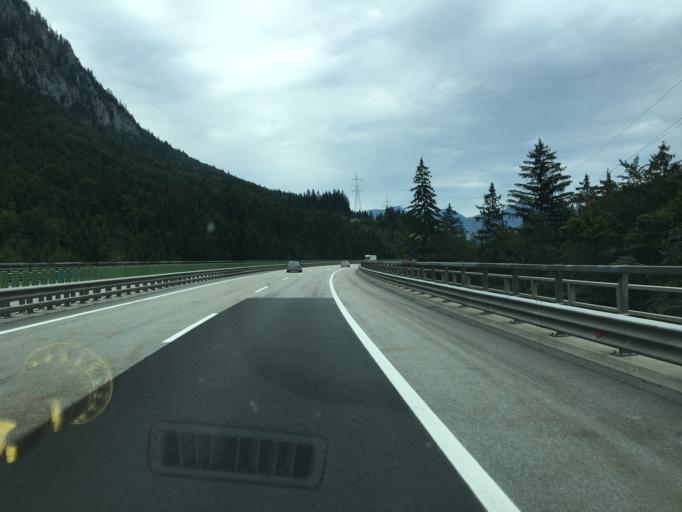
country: AT
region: Styria
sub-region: Politischer Bezirk Liezen
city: Ardning
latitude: 47.6405
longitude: 14.3293
